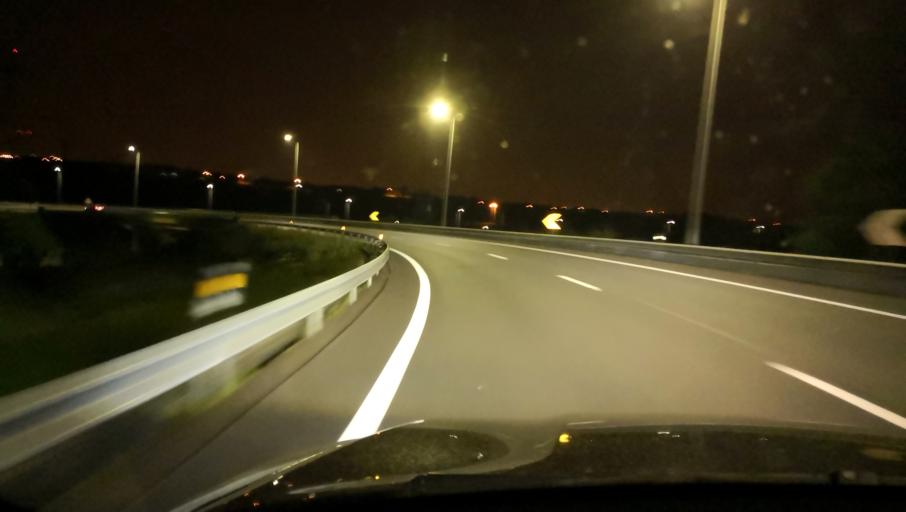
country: PT
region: Setubal
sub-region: Palmela
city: Palmela
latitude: 38.5821
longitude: -8.8620
